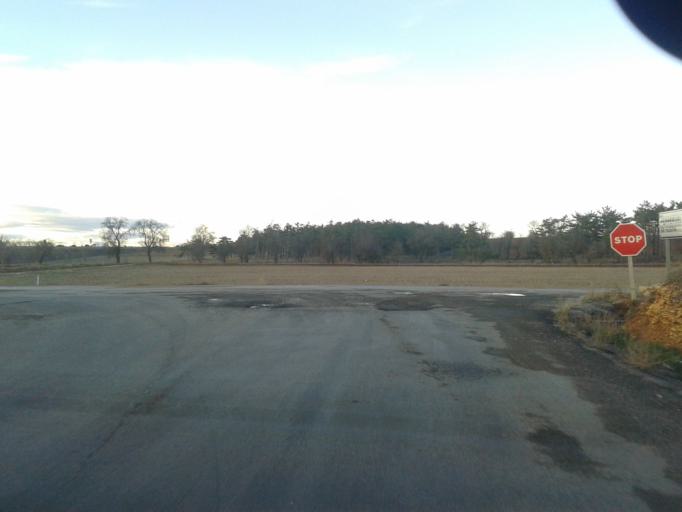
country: ES
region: Aragon
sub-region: Provincia de Zaragoza
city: Lechon
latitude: 41.0512
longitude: -1.2756
